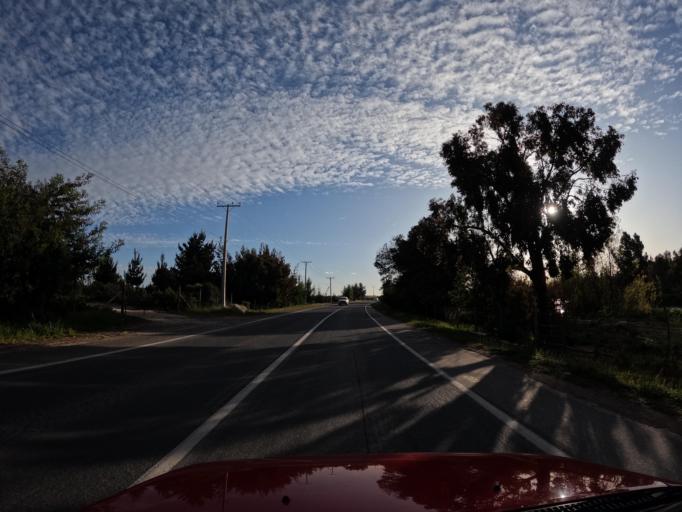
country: CL
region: Valparaiso
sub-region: San Antonio Province
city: San Antonio
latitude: -34.0844
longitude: -71.6668
